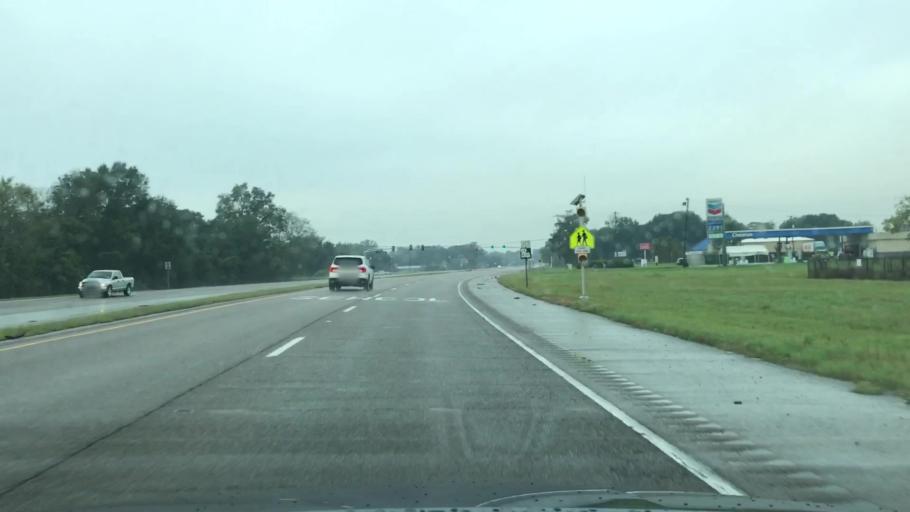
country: US
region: Louisiana
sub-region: Saint Charles Parish
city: Des Allemands
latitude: 29.8257
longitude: -90.4637
